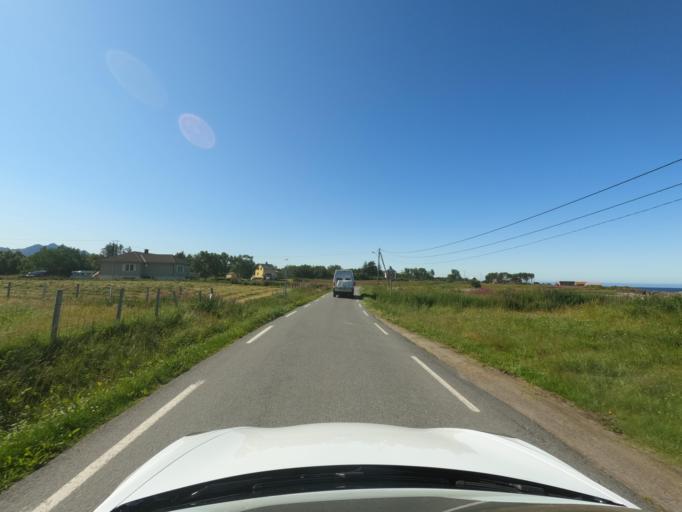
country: NO
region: Nordland
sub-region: Vagan
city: Svolvaer
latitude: 68.3934
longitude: 14.4804
